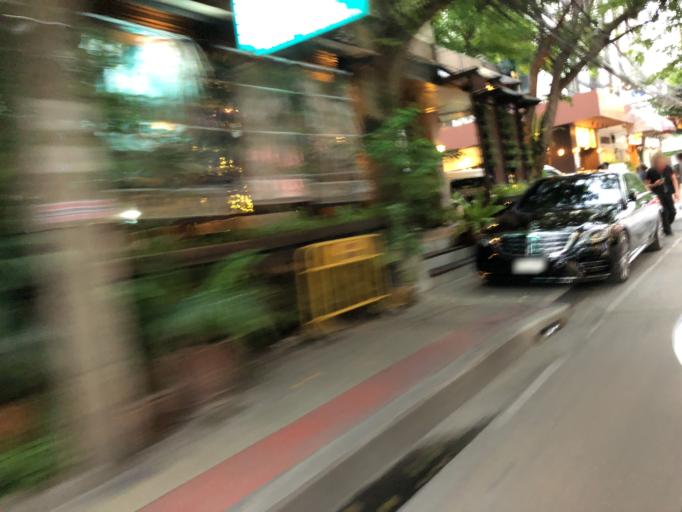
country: TH
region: Bangkok
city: Watthana
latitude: 13.7329
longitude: 100.5711
